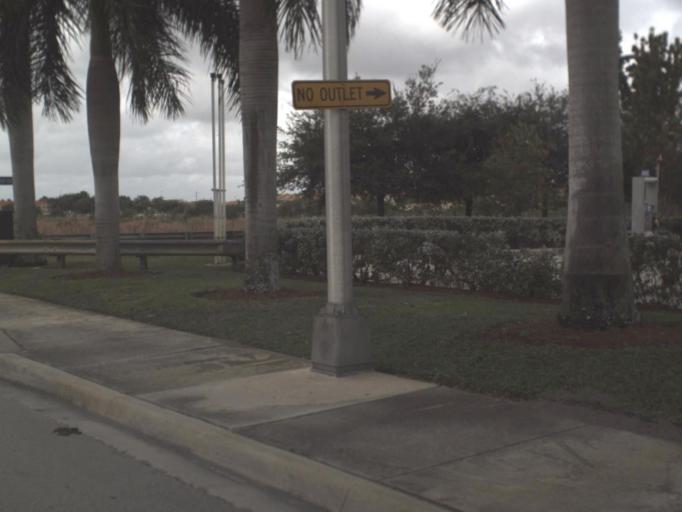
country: US
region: Florida
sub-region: Miami-Dade County
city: Doral
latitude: 25.8118
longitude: -80.3731
